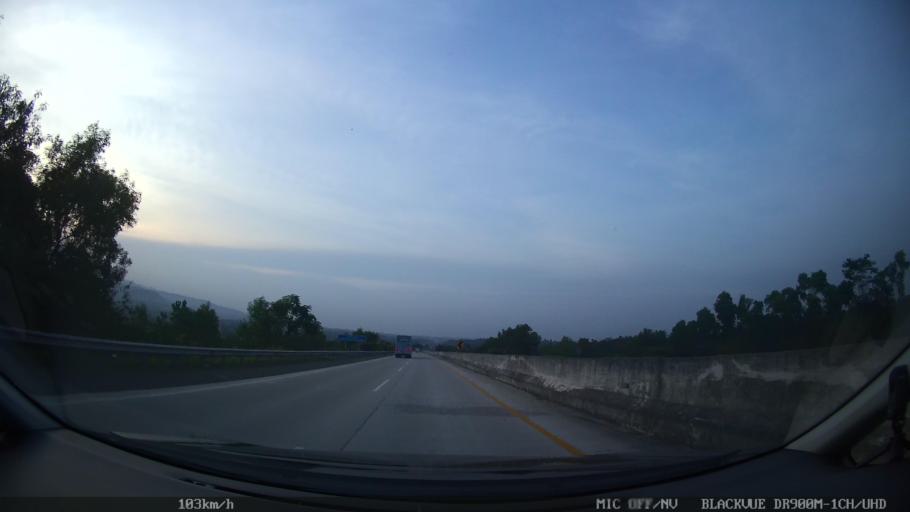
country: ID
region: Lampung
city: Penengahan
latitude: -5.7923
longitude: 105.7265
